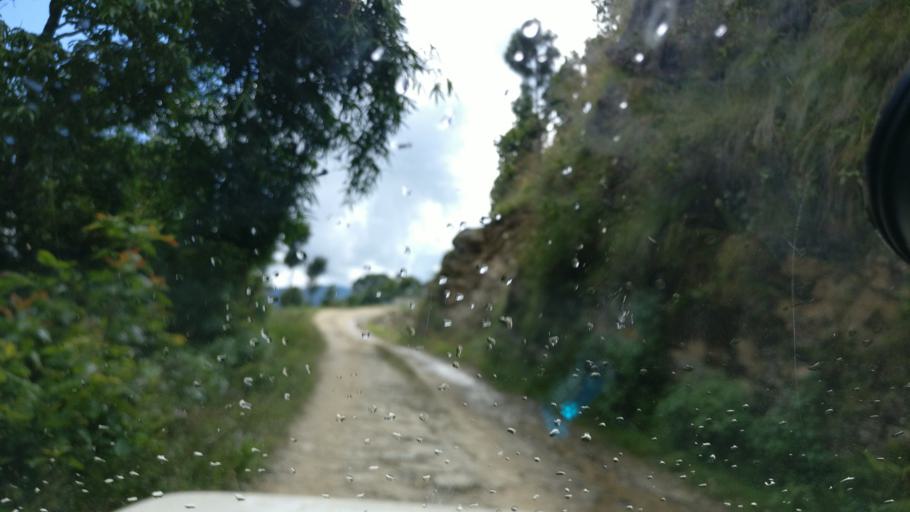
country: NP
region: Western Region
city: Baglung
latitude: 28.2727
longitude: 83.6461
